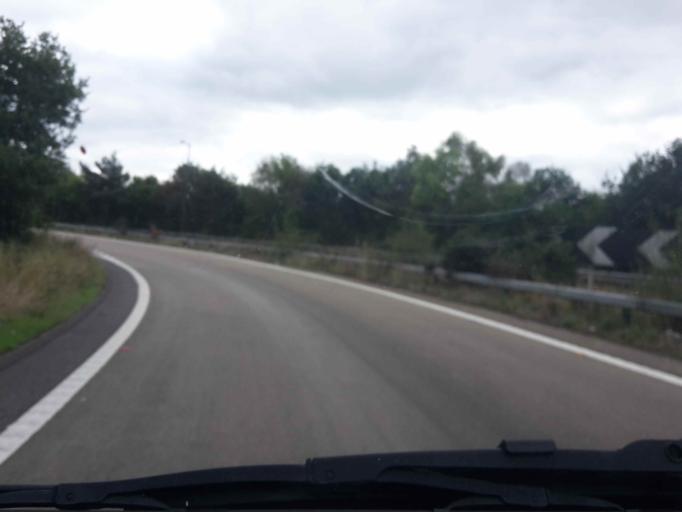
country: GB
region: England
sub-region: Hampshire
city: Fleet
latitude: 51.3009
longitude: -0.7989
